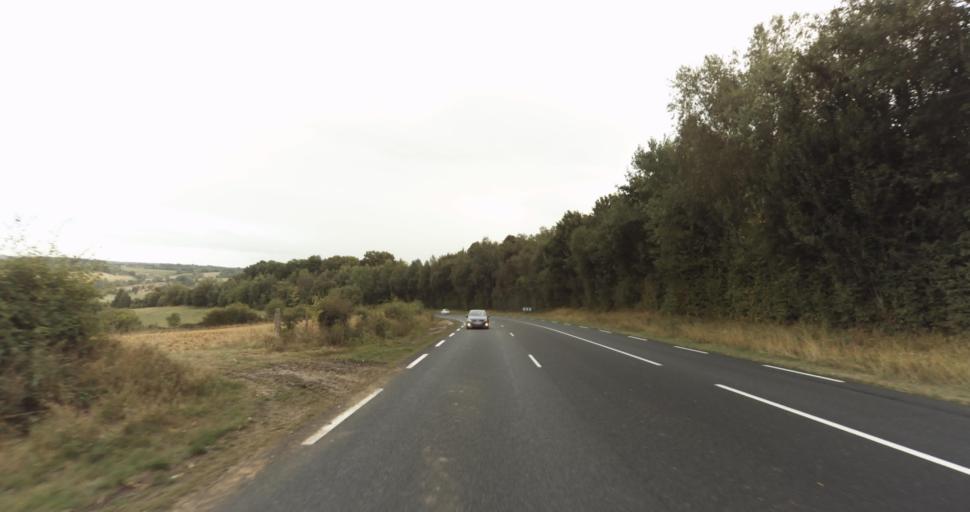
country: FR
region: Lower Normandy
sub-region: Departement de l'Orne
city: Gace
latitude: 48.8480
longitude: 0.2596
